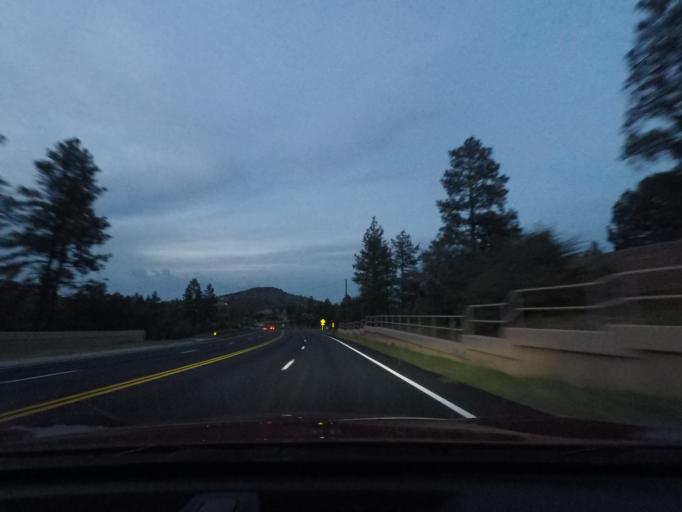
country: US
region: Arizona
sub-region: Yavapai County
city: Prescott
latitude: 34.5863
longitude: -112.4988
